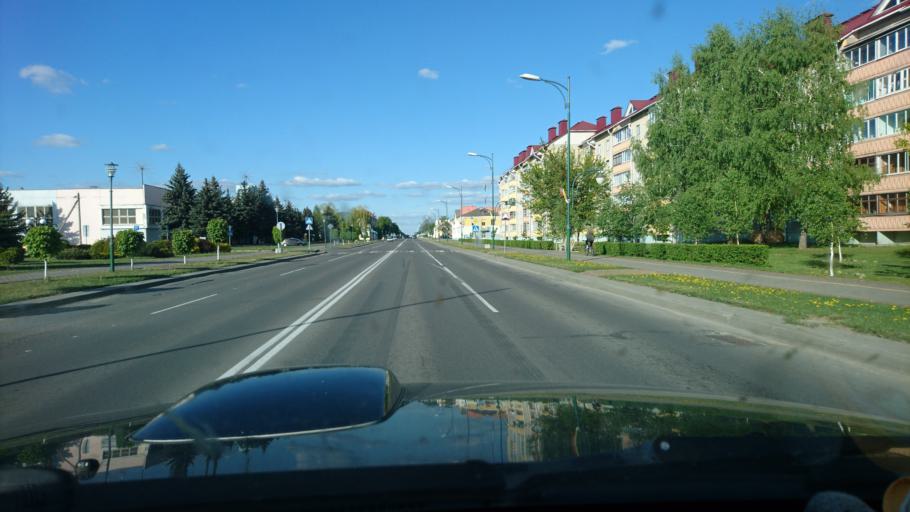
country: BY
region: Brest
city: Byaroza
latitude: 52.5275
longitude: 24.9711
